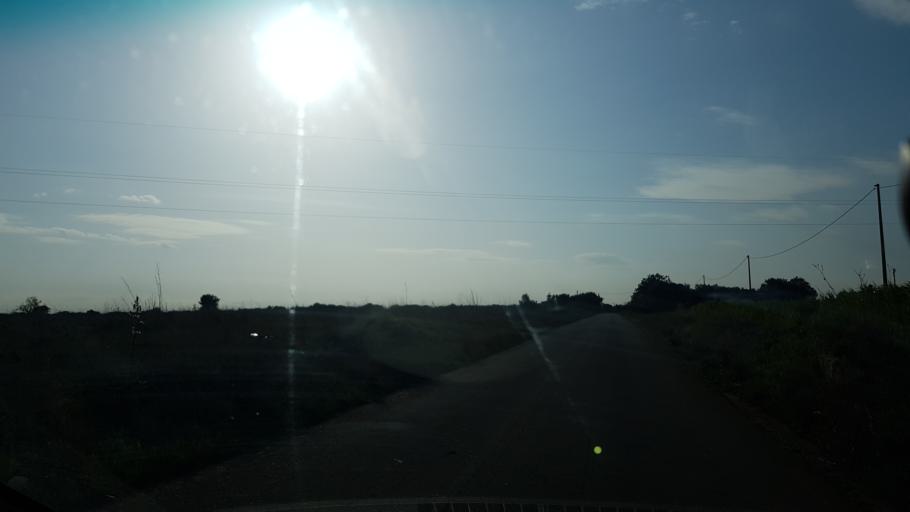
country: IT
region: Apulia
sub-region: Provincia di Brindisi
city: San Vito dei Normanni
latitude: 40.6856
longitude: 17.7710
